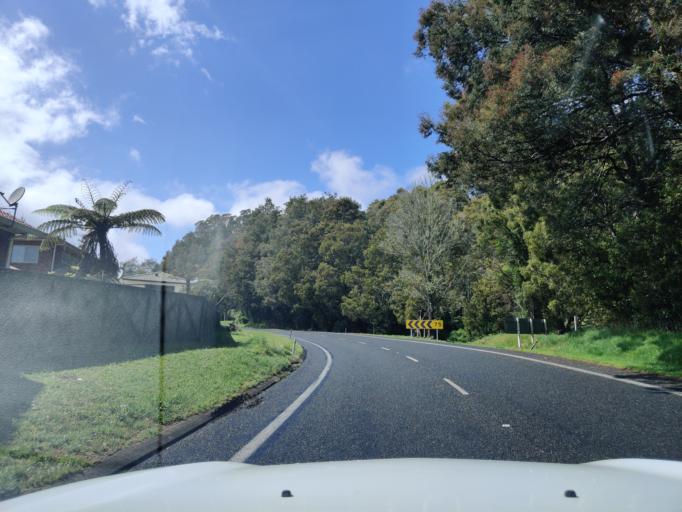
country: NZ
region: Bay of Plenty
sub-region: Rotorua District
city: Rotorua
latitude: -38.1573
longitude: 176.2928
